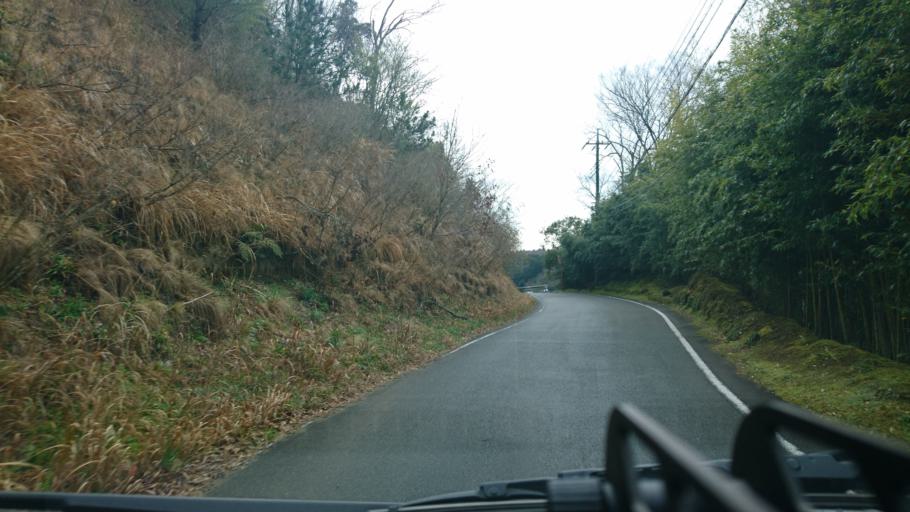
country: JP
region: Chiba
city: Kimitsu
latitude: 35.2966
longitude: 139.9613
